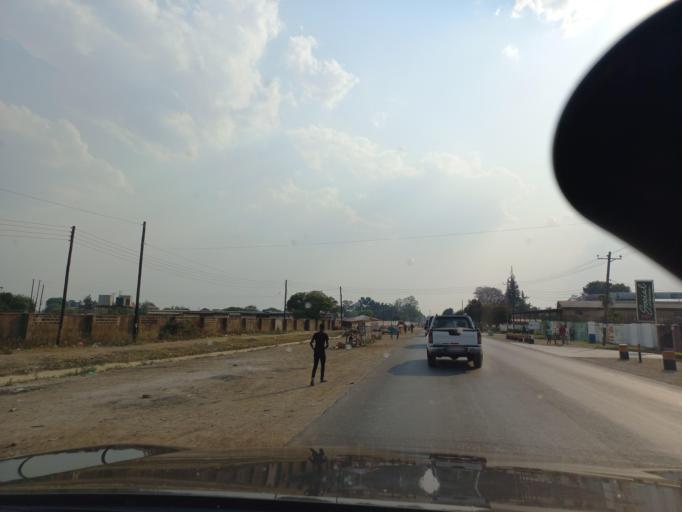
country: ZM
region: Lusaka
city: Lusaka
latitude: -15.4556
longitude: 28.2650
